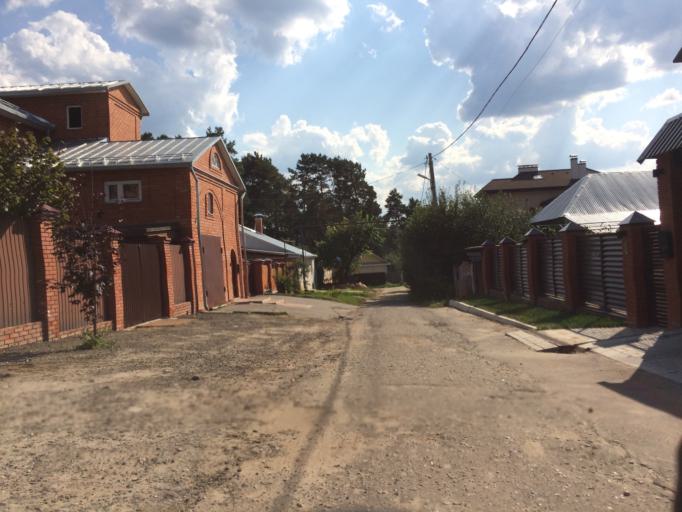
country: RU
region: Mariy-El
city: Yoshkar-Ola
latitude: 56.6183
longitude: 47.9476
